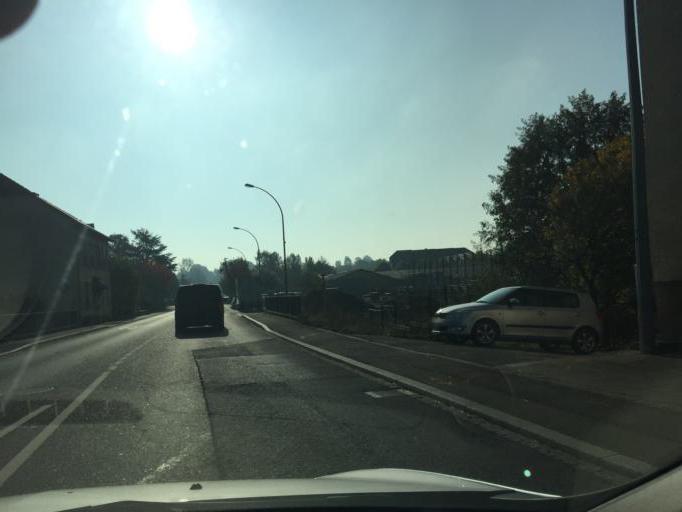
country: LU
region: Luxembourg
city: Moutfort
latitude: 49.5891
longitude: 6.2571
